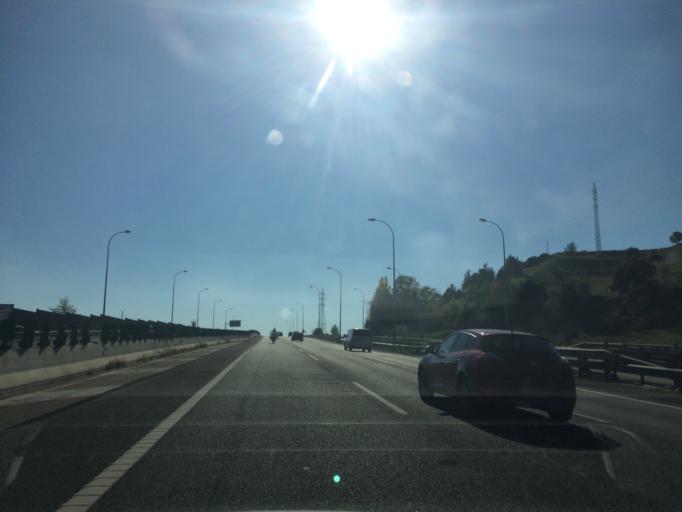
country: ES
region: Madrid
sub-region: Provincia de Madrid
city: San Sebastian de los Reyes
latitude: 40.5833
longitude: -3.5845
